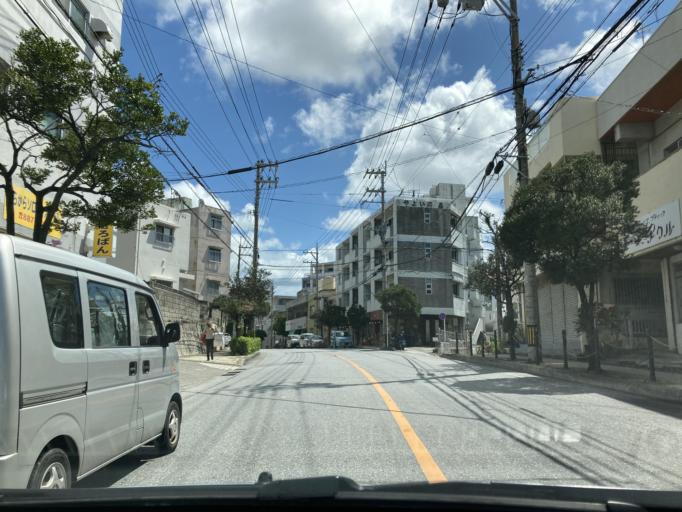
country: JP
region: Okinawa
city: Naha-shi
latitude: 26.2174
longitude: 127.7063
